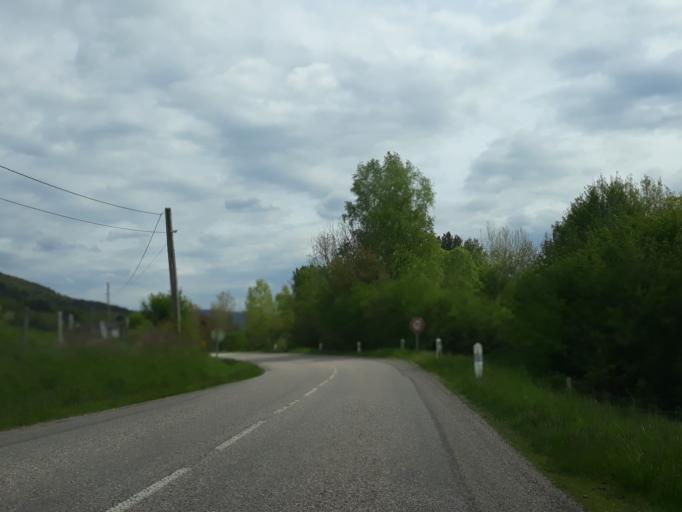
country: FR
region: Lorraine
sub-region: Departement des Vosges
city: Granges-sur-Vologne
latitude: 48.1729
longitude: 6.7720
